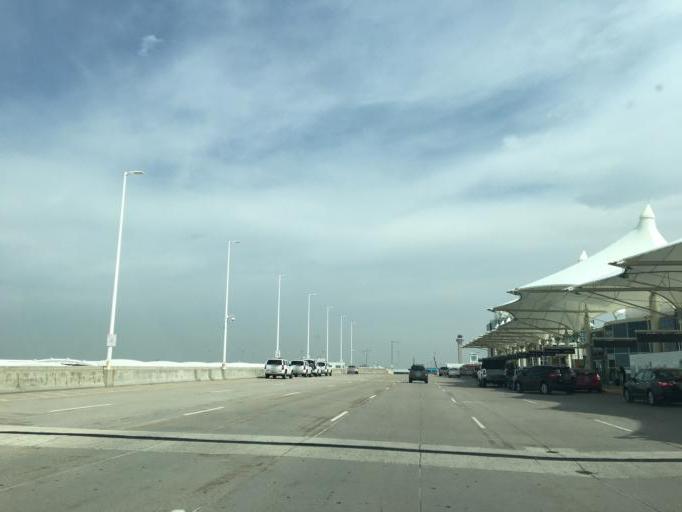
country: US
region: Colorado
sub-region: Weld County
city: Lochbuie
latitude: 39.8493
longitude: -104.6750
